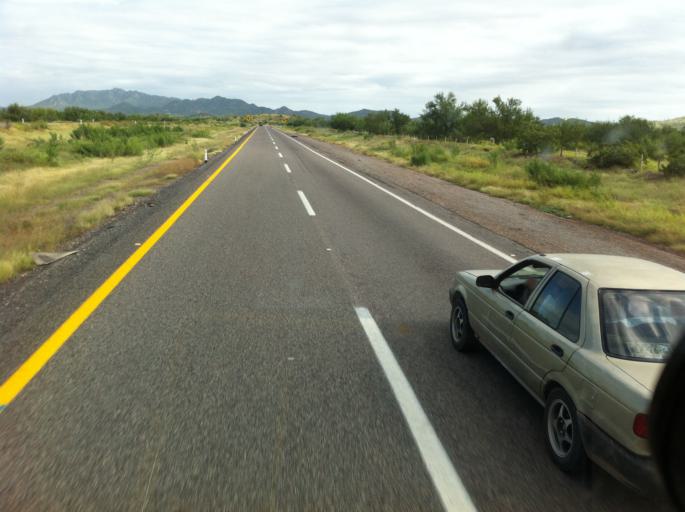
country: MX
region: Sonora
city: Hermosillo
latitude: 28.8905
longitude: -110.9539
